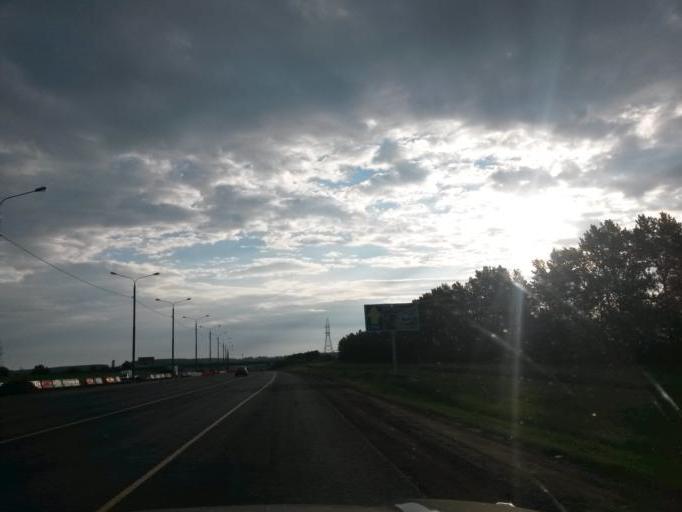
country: RU
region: Moskovskaya
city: Klimovsk
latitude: 55.3406
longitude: 37.5821
